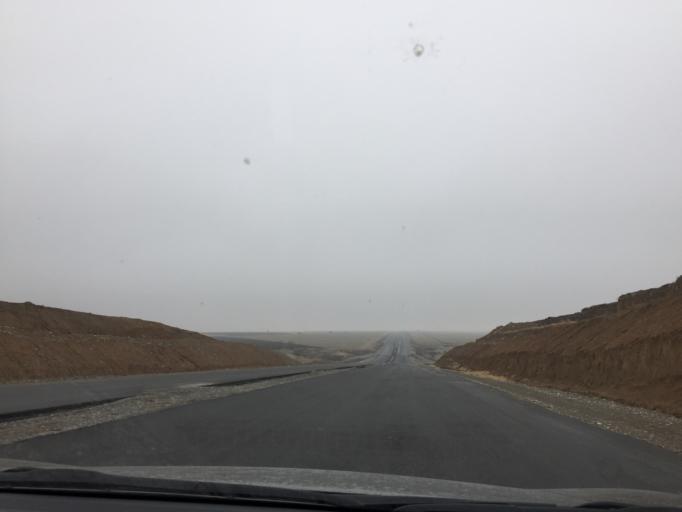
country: KZ
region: Ongtustik Qazaqstan
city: Turar Ryskulov
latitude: 42.5081
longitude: 70.4088
